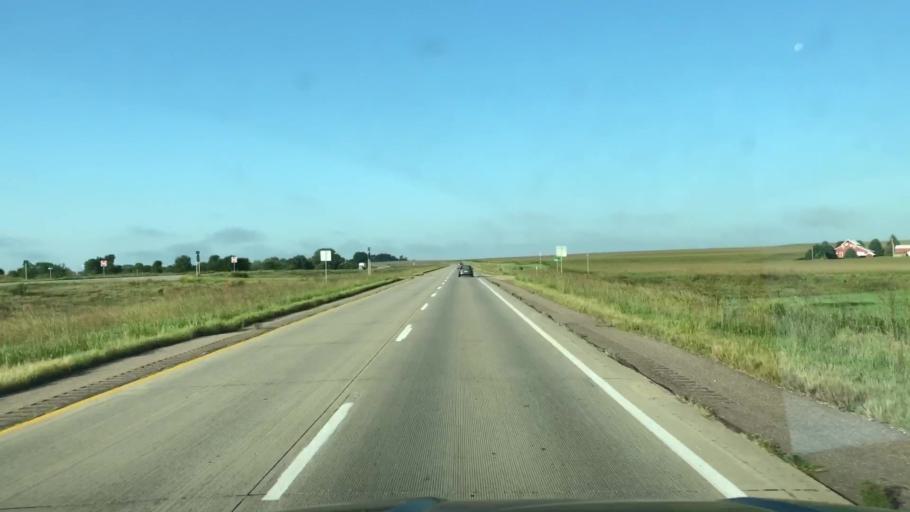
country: US
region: Iowa
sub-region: Sioux County
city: Alton
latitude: 42.9239
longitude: -96.0643
